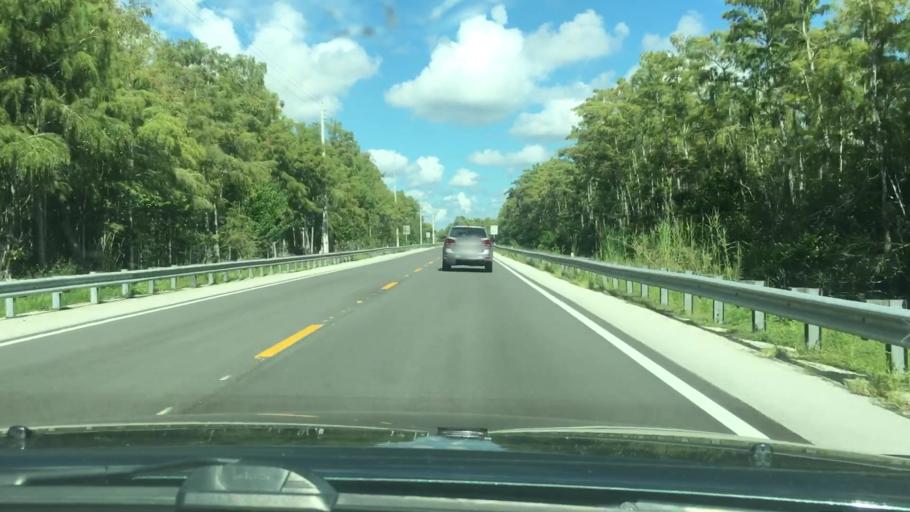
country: US
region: Florida
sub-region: Miami-Dade County
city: Kendall West
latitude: 25.8029
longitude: -80.8703
